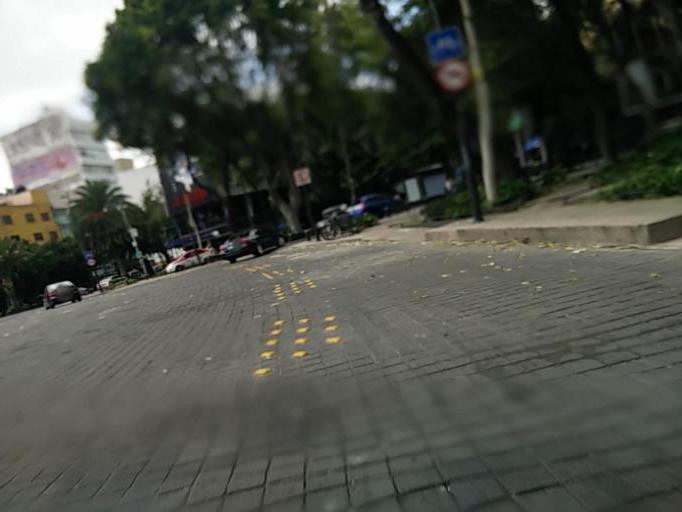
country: MX
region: Mexico City
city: Benito Juarez
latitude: 19.4203
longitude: -99.1667
